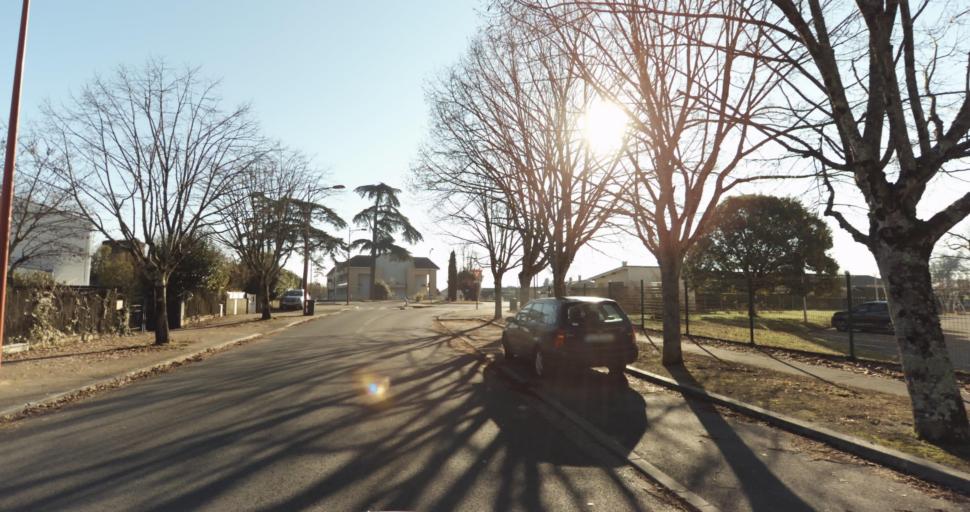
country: FR
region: Aquitaine
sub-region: Departement de la Gironde
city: Bassens
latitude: 44.8917
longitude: -0.5136
